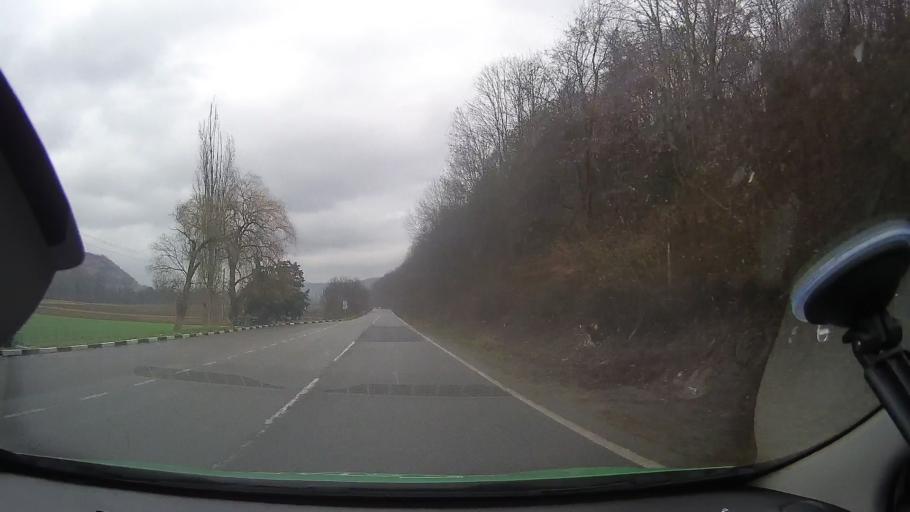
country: RO
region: Arad
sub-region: Comuna Buteni
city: Buteni
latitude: 46.3057
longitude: 22.1530
